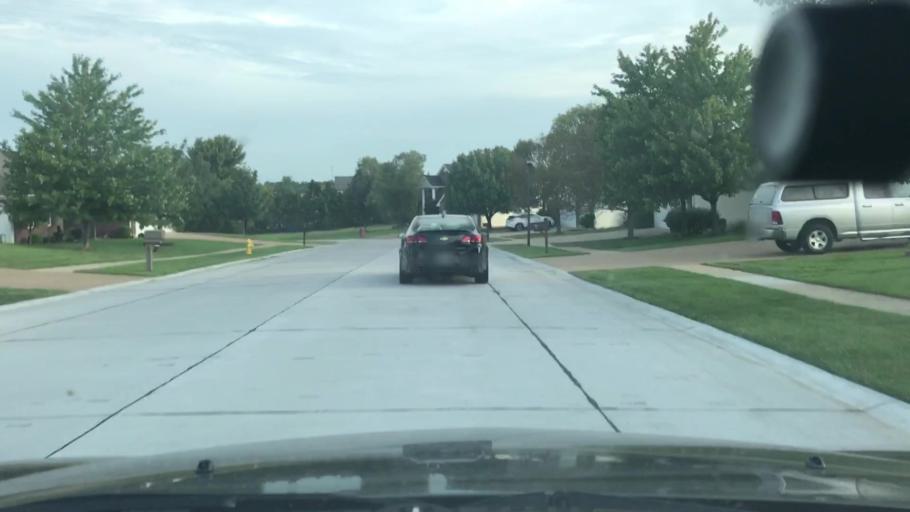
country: US
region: Missouri
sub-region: Saint Charles County
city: Wentzville
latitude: 38.8164
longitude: -90.8903
